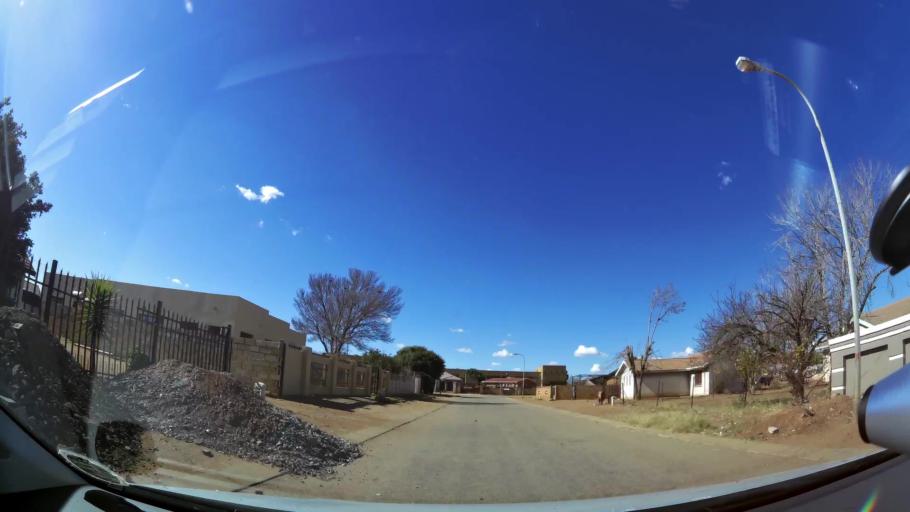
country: ZA
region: North-West
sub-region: Dr Kenneth Kaunda District Municipality
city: Klerksdorp
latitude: -26.8739
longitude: 26.5849
